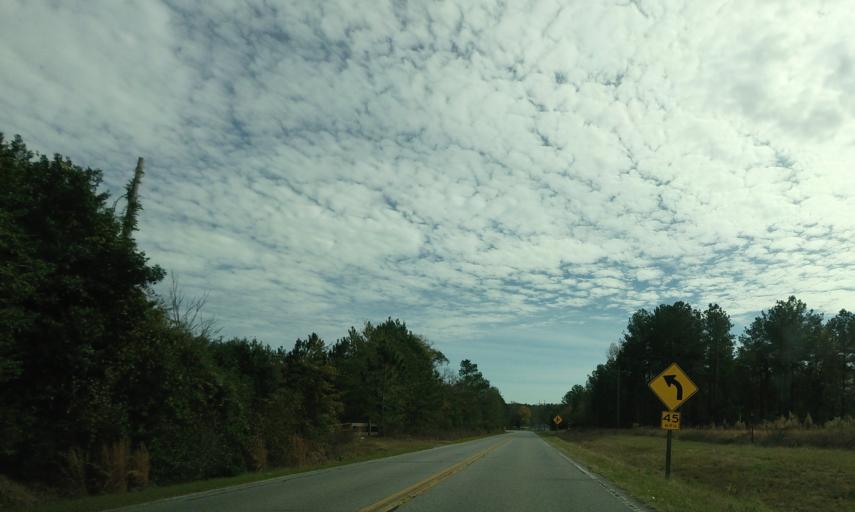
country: US
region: Georgia
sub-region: Bleckley County
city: Cochran
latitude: 32.3966
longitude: -83.3175
